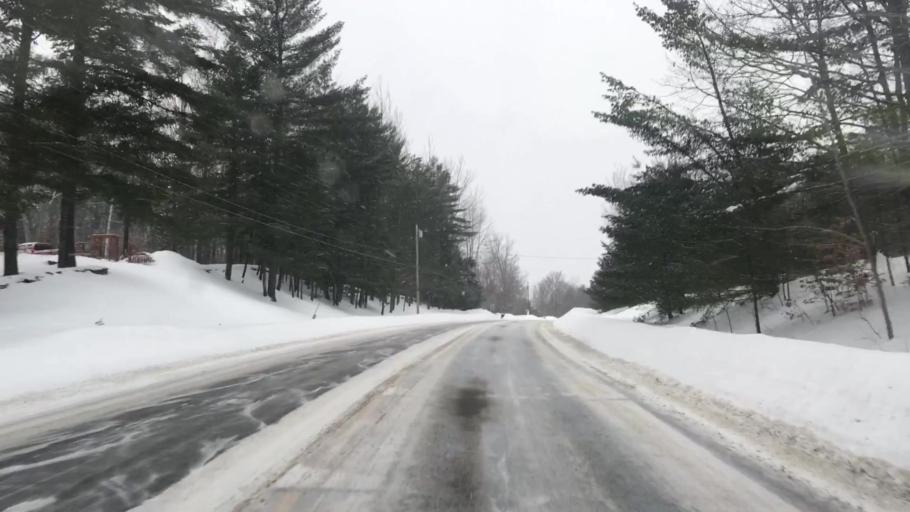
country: US
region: Maine
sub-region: Penobscot County
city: Medway
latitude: 45.5224
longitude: -68.3543
